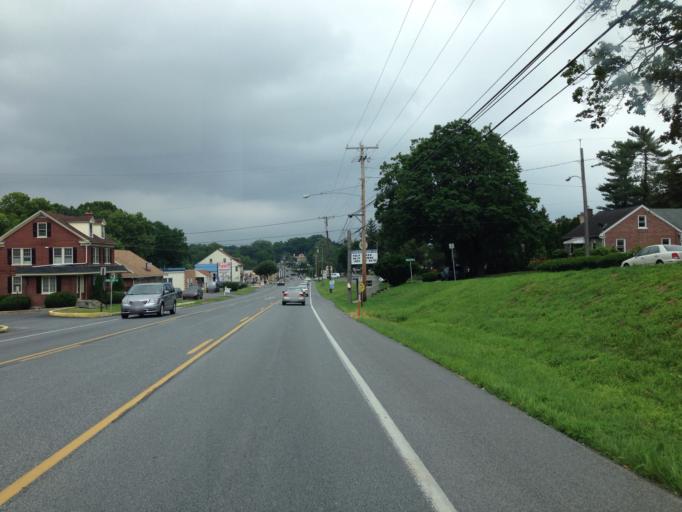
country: US
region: Pennsylvania
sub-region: Lancaster County
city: Millersville
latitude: 40.0380
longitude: -76.3484
